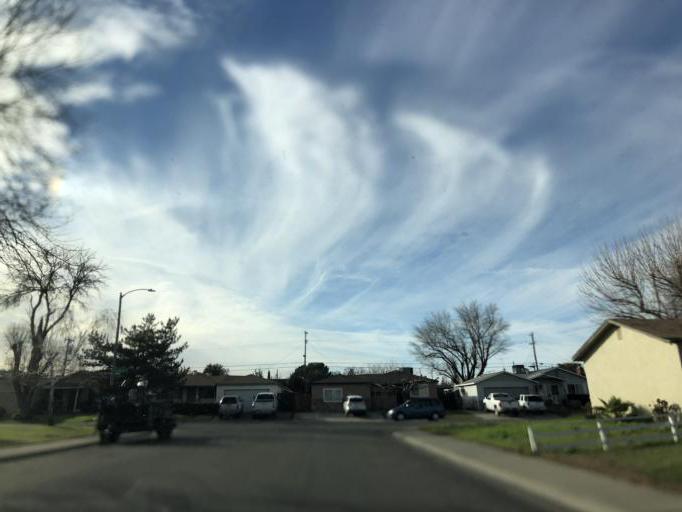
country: US
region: California
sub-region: Yolo County
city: Woodland
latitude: 38.6722
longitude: -121.7621
